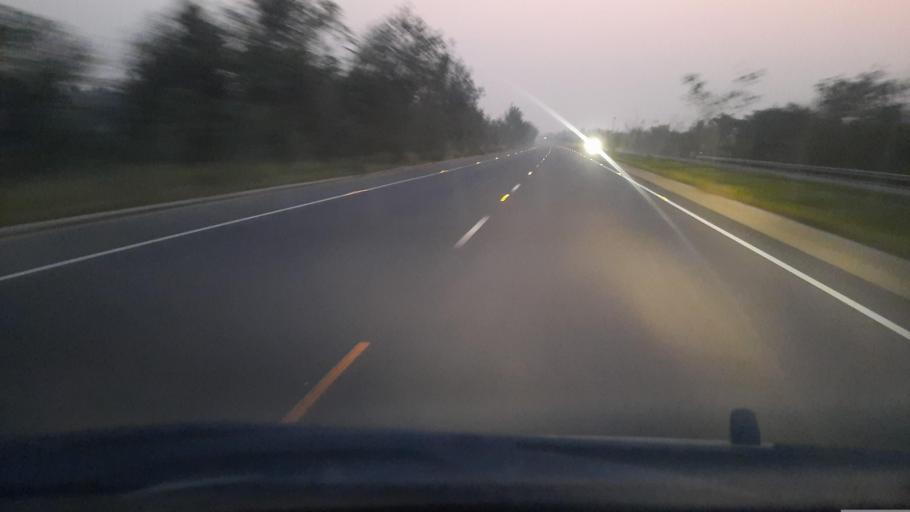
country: BD
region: Dhaka
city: Char Bhadrasan
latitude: 23.3983
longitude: 90.2234
